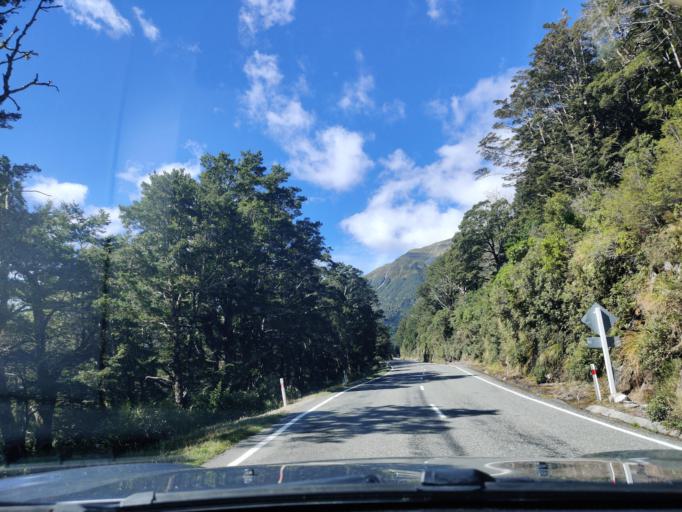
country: NZ
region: Canterbury
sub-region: Hurunui District
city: Amberley
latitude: -42.3747
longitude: 172.3904
